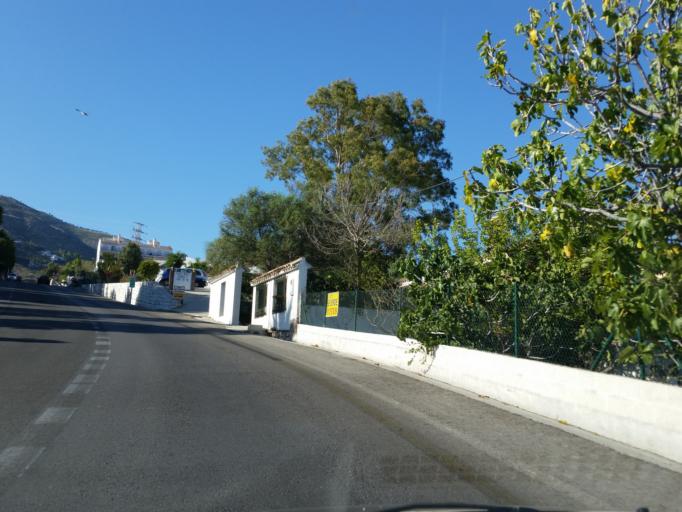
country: ES
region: Andalusia
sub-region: Provincia de Malaga
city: Mijas
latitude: 36.5775
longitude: -4.6364
